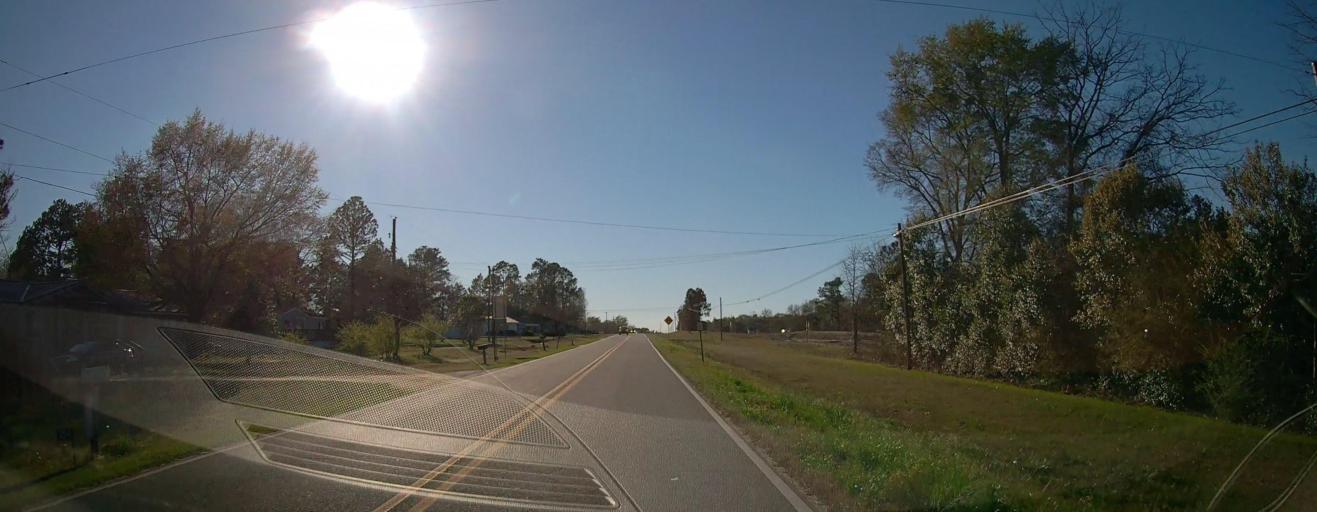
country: US
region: Georgia
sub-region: Taylor County
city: Butler
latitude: 32.5557
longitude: -84.2159
